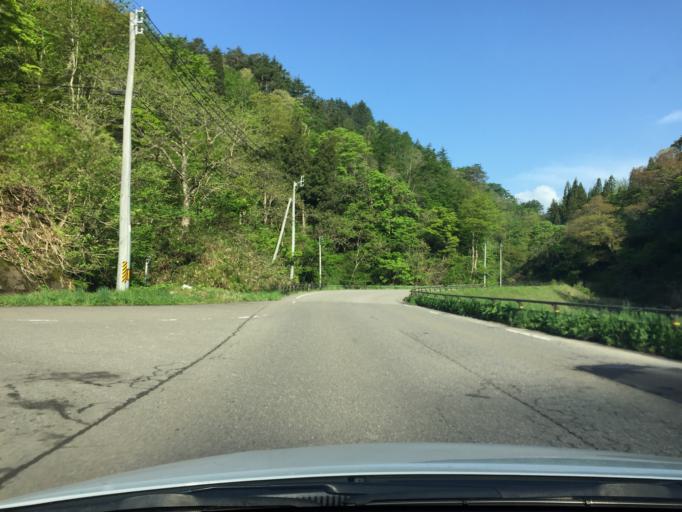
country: JP
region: Fukushima
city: Kitakata
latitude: 37.6754
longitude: 139.7267
